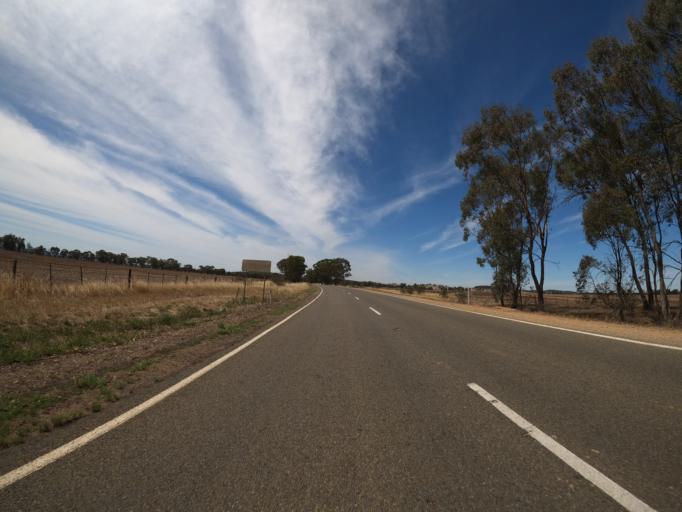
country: AU
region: Victoria
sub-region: Benalla
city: Benalla
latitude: -36.2994
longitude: 145.9527
